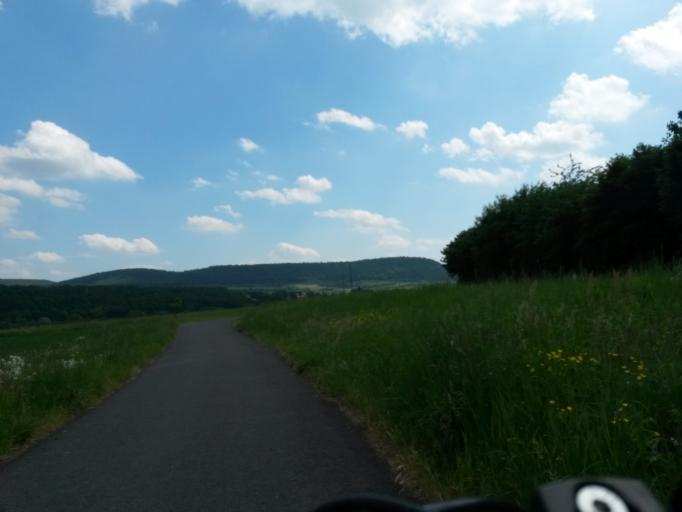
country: DE
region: Bavaria
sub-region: Regierungsbezirk Unterfranken
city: Euerdorf
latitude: 50.1626
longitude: 10.0157
